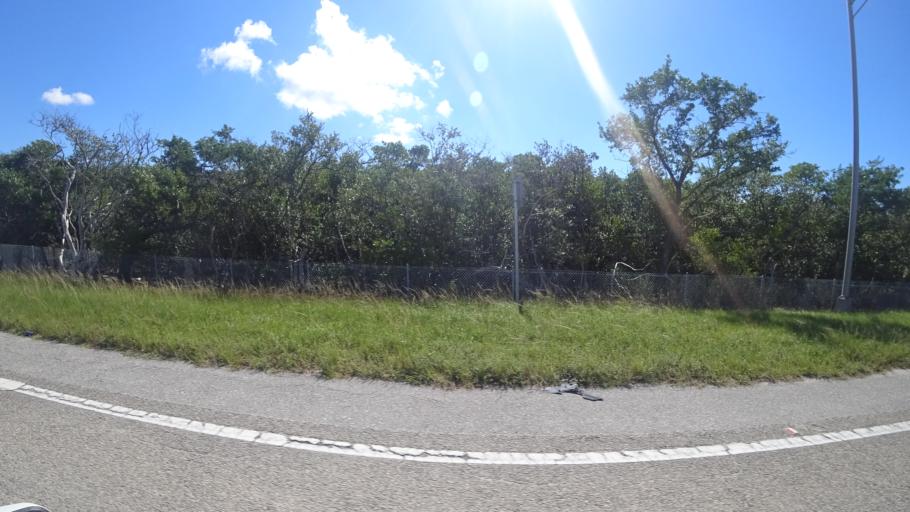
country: US
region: Florida
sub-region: Manatee County
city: Memphis
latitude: 27.5832
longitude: -82.6111
